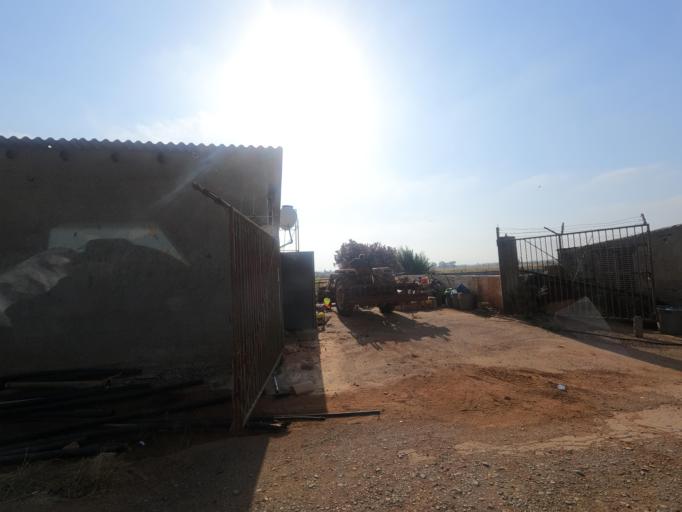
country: CY
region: Ammochostos
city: Avgorou
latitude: 35.0520
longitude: 33.8190
